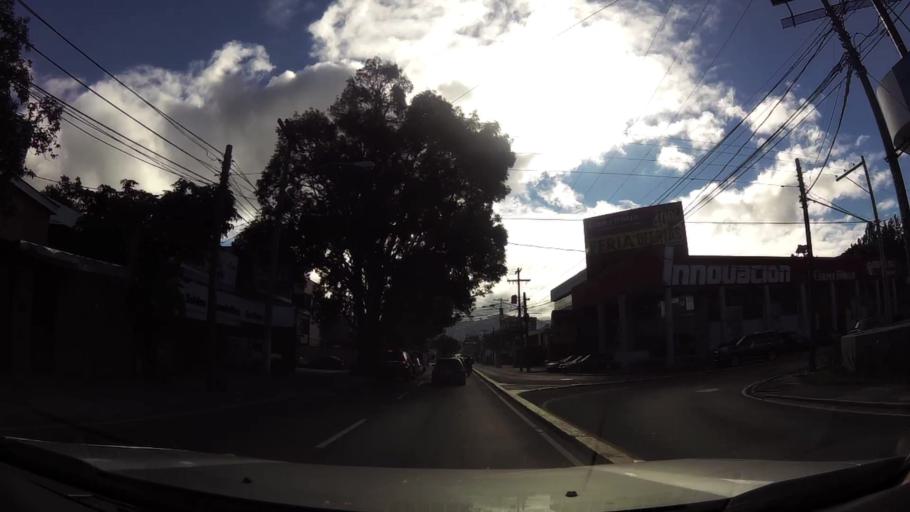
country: GT
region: Guatemala
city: Santa Catarina Pinula
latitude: 14.5901
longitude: -90.5103
